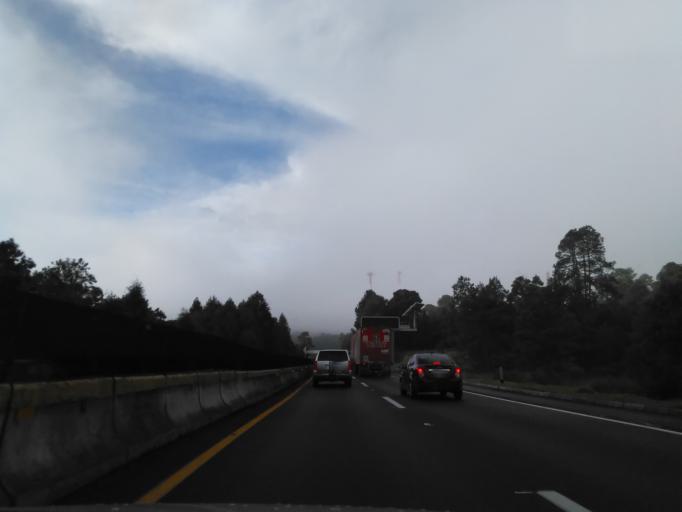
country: MX
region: Morelos
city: Tres Marias
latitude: 19.0921
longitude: -99.2135
